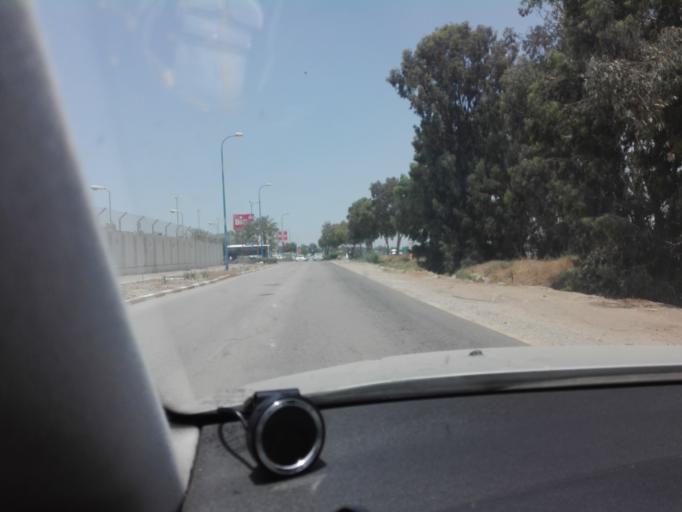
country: IL
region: Central District
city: Bene 'Ayish
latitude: 31.7260
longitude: 34.7552
